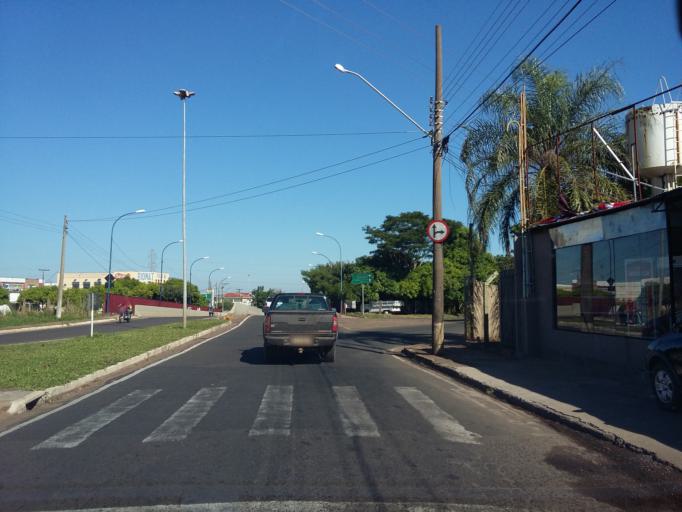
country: BR
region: Sao Paulo
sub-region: Sao Jose Do Rio Preto
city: Sao Jose do Rio Preto
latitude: -20.8410
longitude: -49.3708
